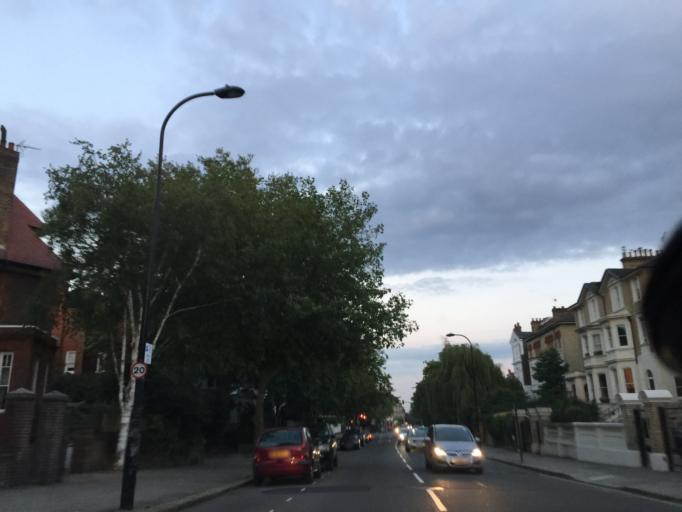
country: GB
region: England
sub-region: Greater London
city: Belsize Park
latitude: 51.5540
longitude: -0.1707
